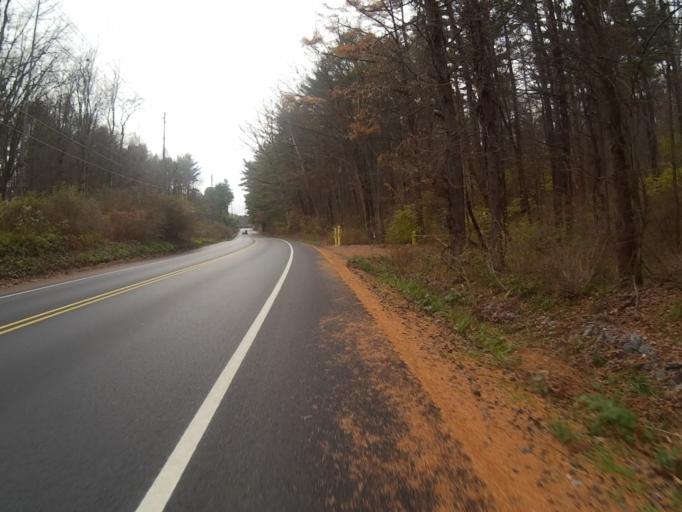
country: US
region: Pennsylvania
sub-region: Centre County
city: State College
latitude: 40.8259
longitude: -77.8707
